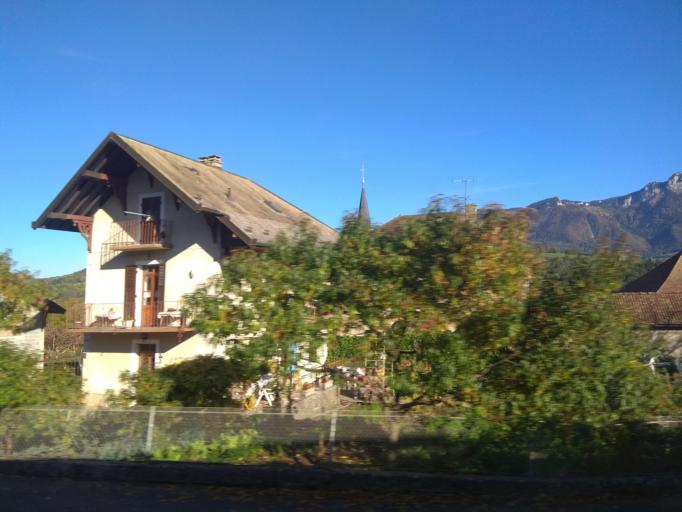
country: FR
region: Rhone-Alpes
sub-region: Departement de la Haute-Savoie
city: Saint-Martin-Bellevue
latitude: 45.9769
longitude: 6.1572
